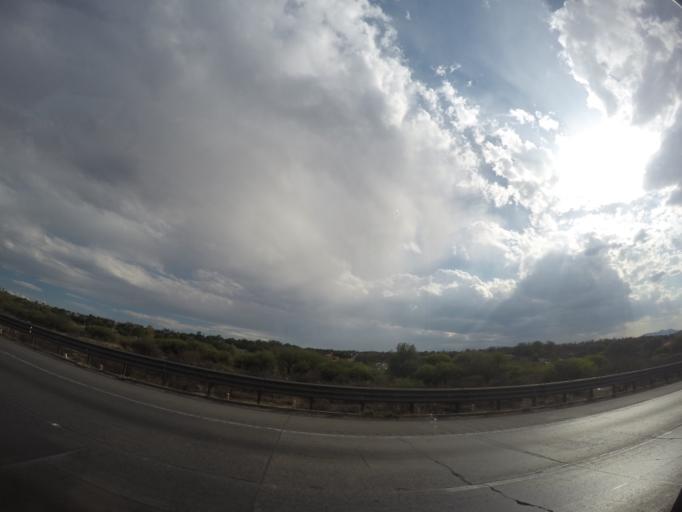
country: MX
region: Mexico
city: San Francisco Soyaniquilpan
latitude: 20.0115
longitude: -99.5112
